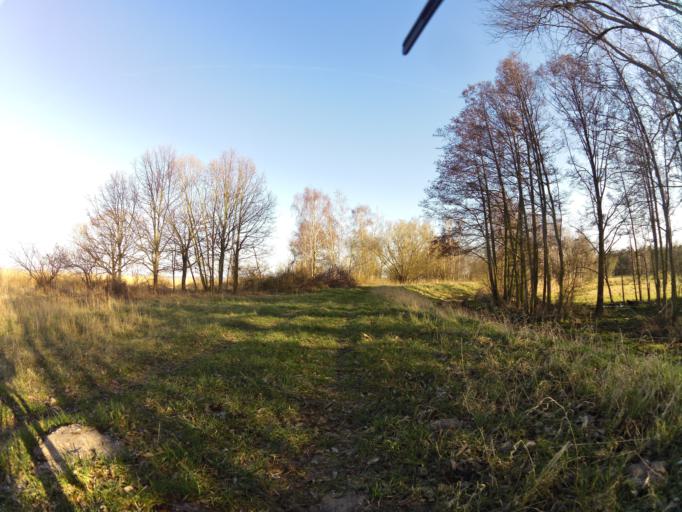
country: PL
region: West Pomeranian Voivodeship
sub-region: Powiat policki
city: Nowe Warpno
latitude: 53.7216
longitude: 14.3383
